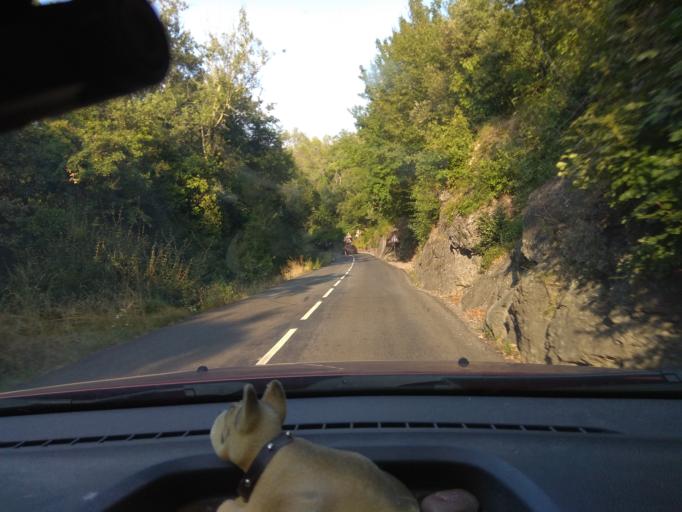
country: FR
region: Provence-Alpes-Cote d'Azur
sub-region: Departement des Alpes-Maritimes
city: Tourrettes-sur-Loup
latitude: 43.6826
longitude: 7.0550
